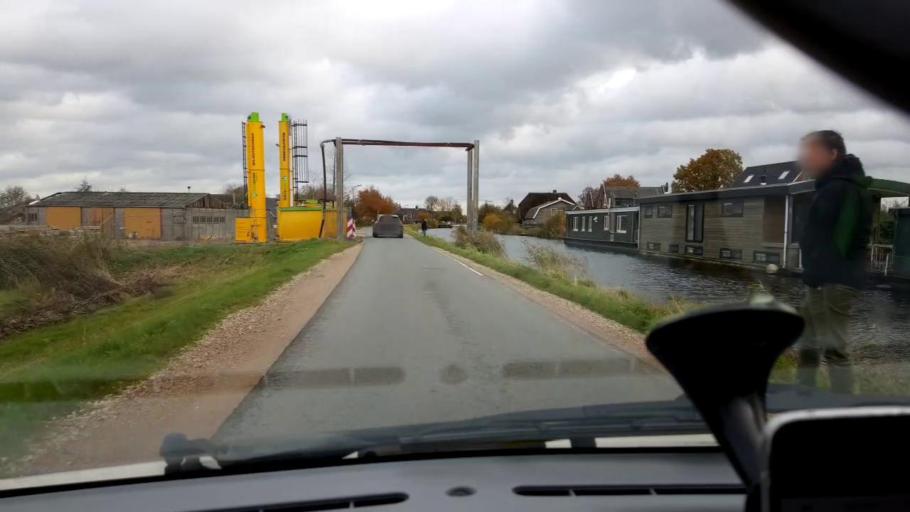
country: NL
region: Utrecht
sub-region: Gemeente De Ronde Venen
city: Mijdrecht
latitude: 52.1626
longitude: 4.9115
